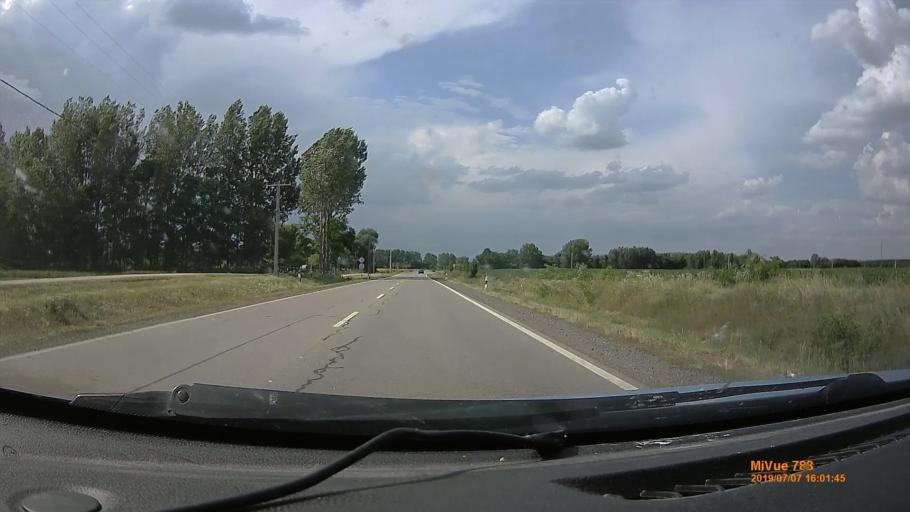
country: HU
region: Heves
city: Boldog
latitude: 47.6147
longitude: 19.7350
